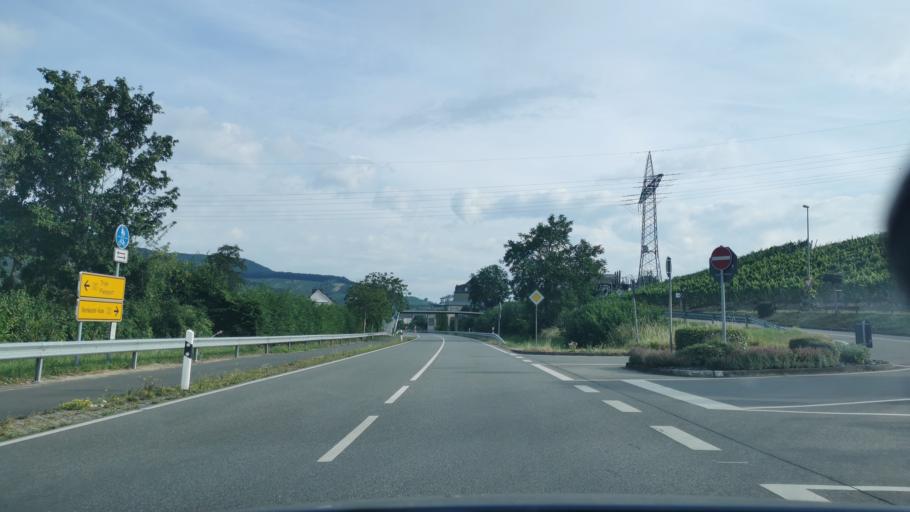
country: DE
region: Rheinland-Pfalz
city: Wintrich
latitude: 49.8770
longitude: 6.9502
